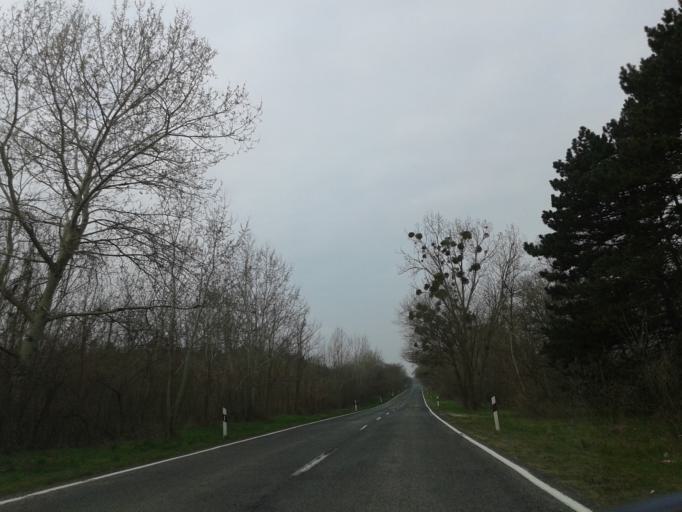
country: HU
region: Gyor-Moson-Sopron
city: Bony
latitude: 47.7317
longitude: 17.8697
